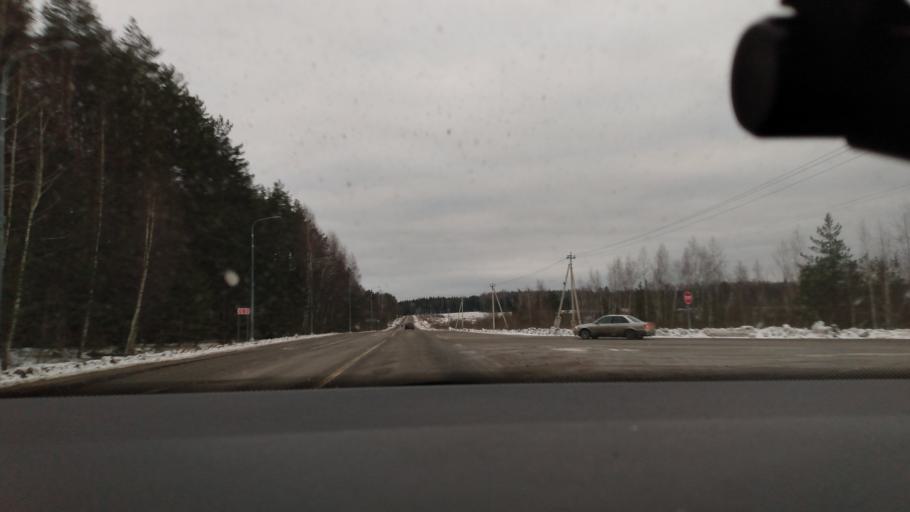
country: RU
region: Moskovskaya
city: Yegor'yevsk
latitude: 55.3356
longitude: 39.0761
